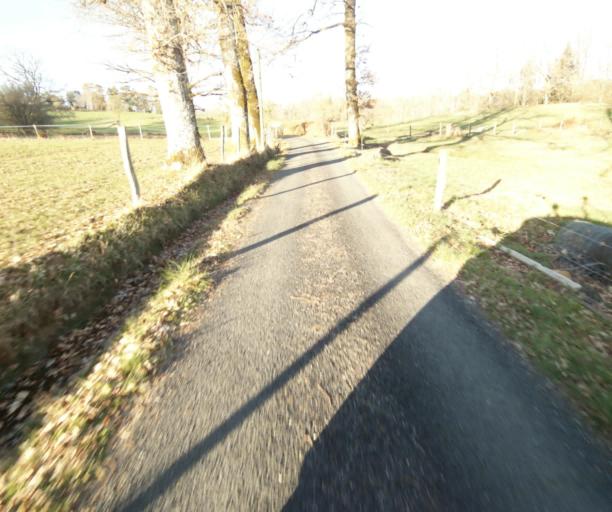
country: FR
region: Limousin
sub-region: Departement de la Correze
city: Saint-Clement
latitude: 45.3680
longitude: 1.6892
